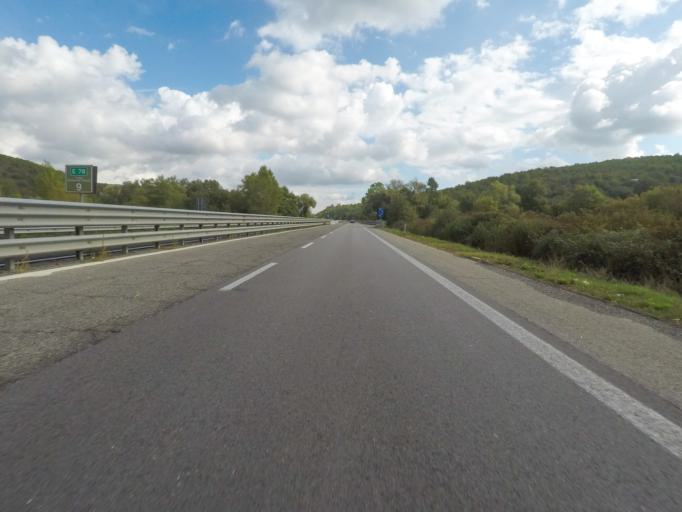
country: IT
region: Tuscany
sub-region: Provincia di Siena
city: Serre di Rapolano
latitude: 43.2479
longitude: 11.6607
